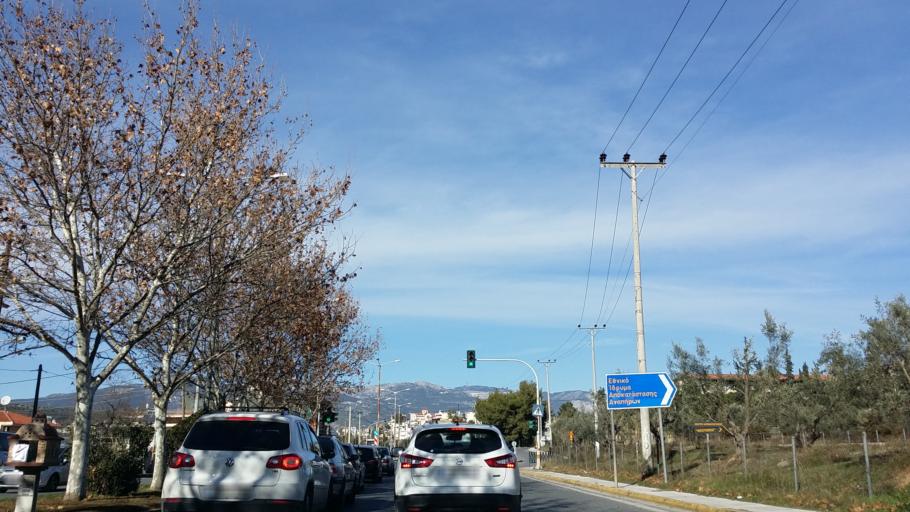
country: GR
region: Attica
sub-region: Nomarchia Athinas
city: Kamateron
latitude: 38.0471
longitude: 23.7157
